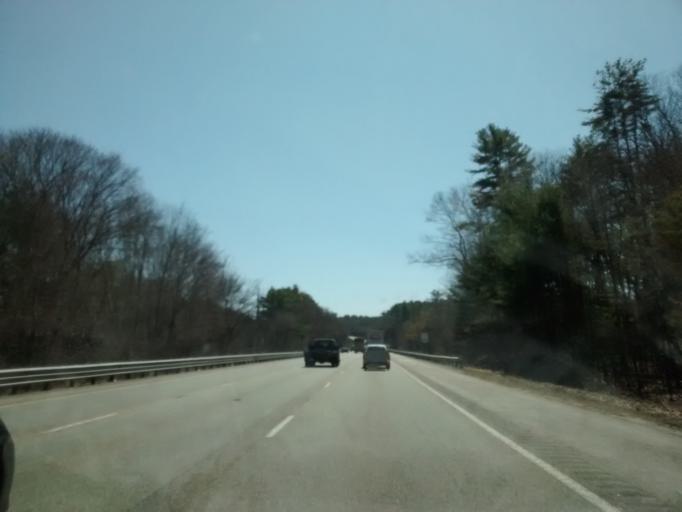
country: US
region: Massachusetts
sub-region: Worcester County
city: Cordaville
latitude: 42.2481
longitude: -71.5571
